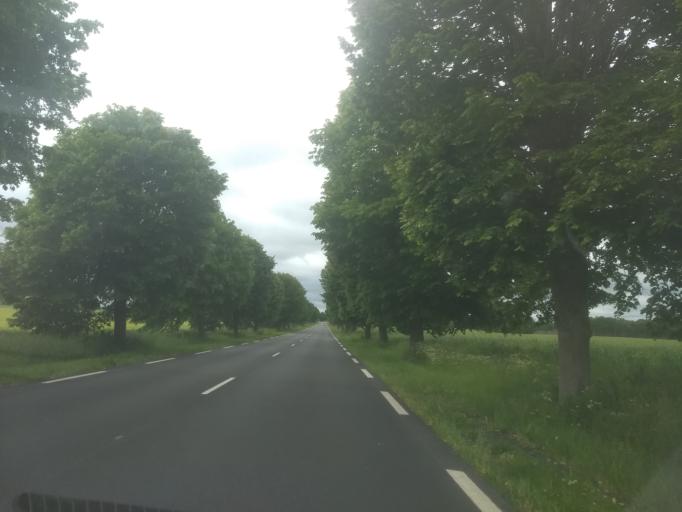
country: FR
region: Centre
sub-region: Departement d'Eure-et-Loir
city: Treon
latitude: 48.6556
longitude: 1.2990
